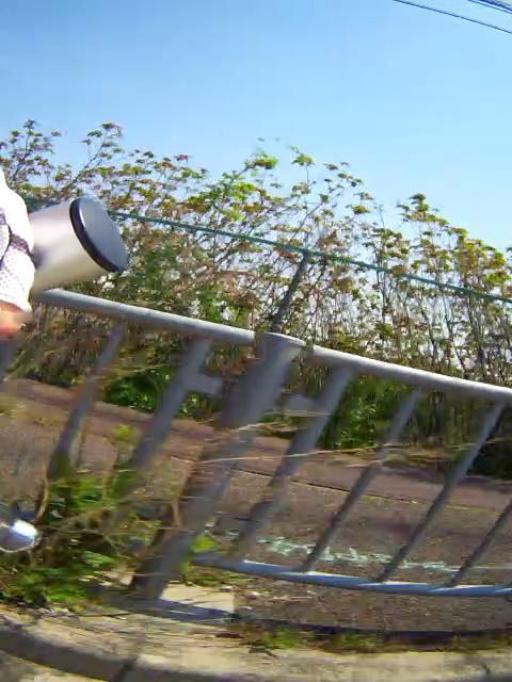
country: JP
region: Osaka
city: Matsubara
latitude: 34.5413
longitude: 135.5585
